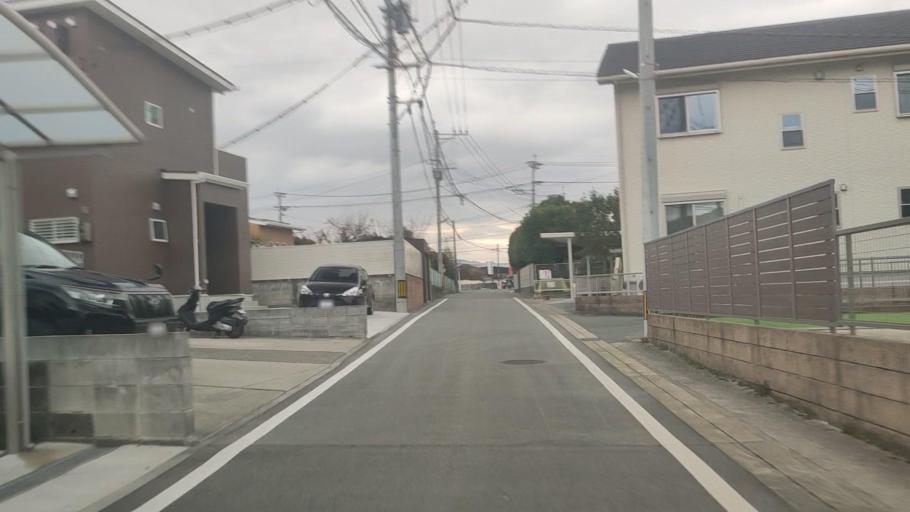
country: JP
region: Kumamoto
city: Ozu
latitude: 32.8282
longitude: 130.8008
